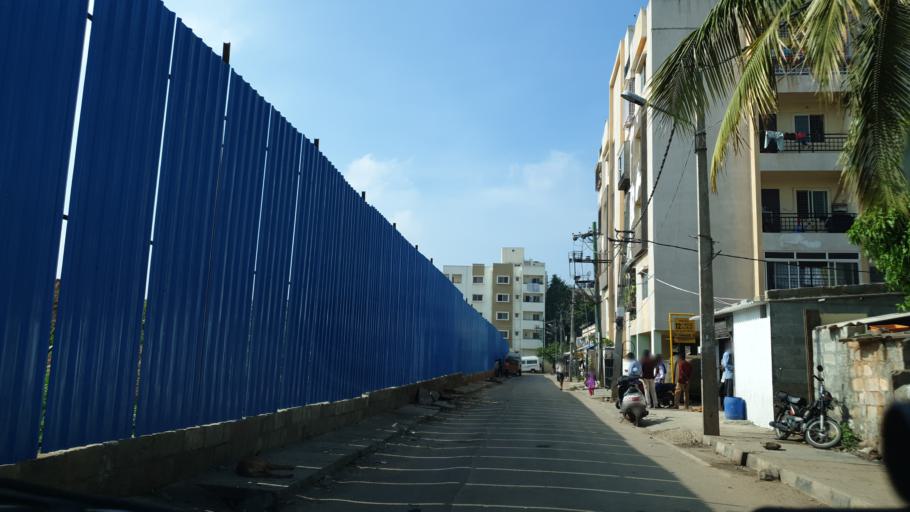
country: IN
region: Karnataka
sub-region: Bangalore Urban
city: Bangalore
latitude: 12.9708
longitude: 77.6704
